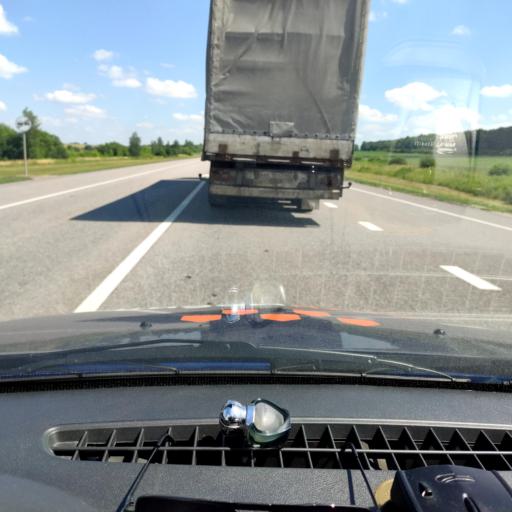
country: RU
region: Orjol
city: Orel
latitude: 52.8564
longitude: 36.2140
